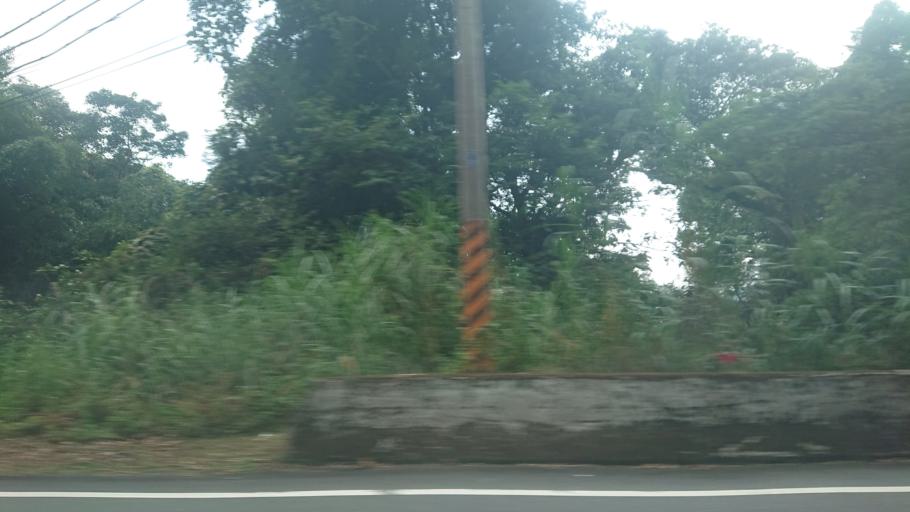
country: TW
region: Taiwan
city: Lugu
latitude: 23.4834
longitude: 120.7406
